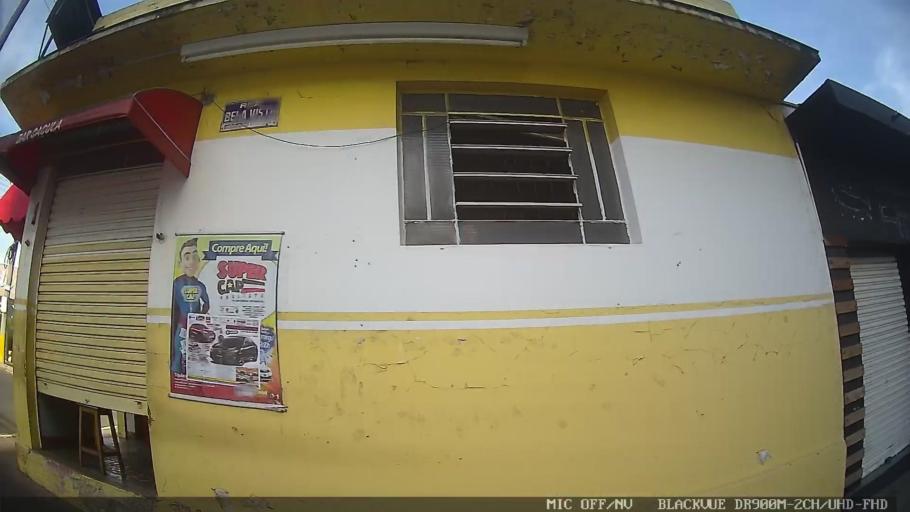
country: BR
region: Sao Paulo
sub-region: Tiete
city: Tiete
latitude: -23.0930
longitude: -47.7179
